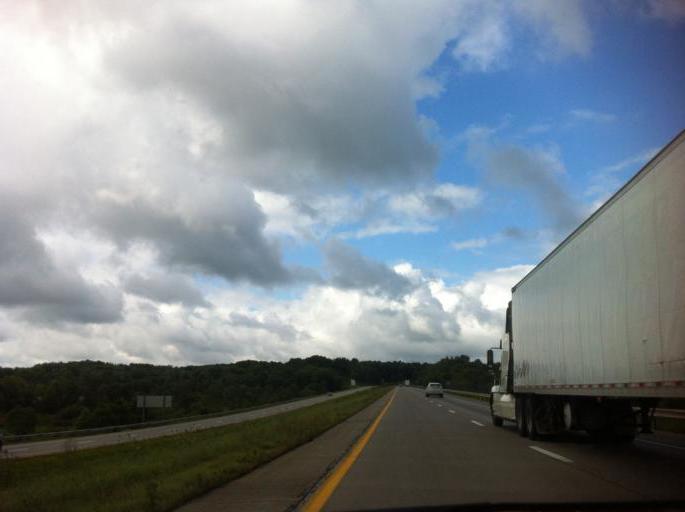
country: US
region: Pennsylvania
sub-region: Mercer County
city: Mercer
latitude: 41.1891
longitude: -80.2552
